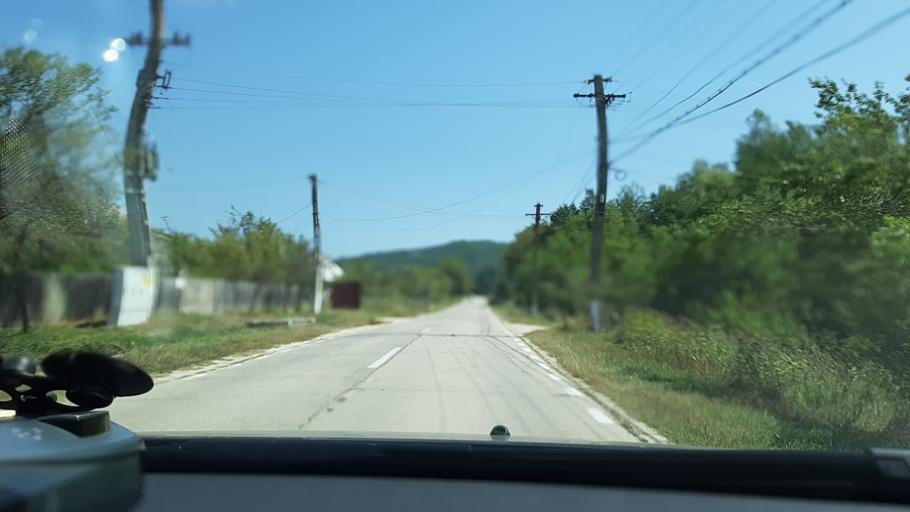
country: RO
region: Gorj
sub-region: Comuna Logresti-Mosteni
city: Logresti Mosteni
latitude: 44.9047
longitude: 23.7433
